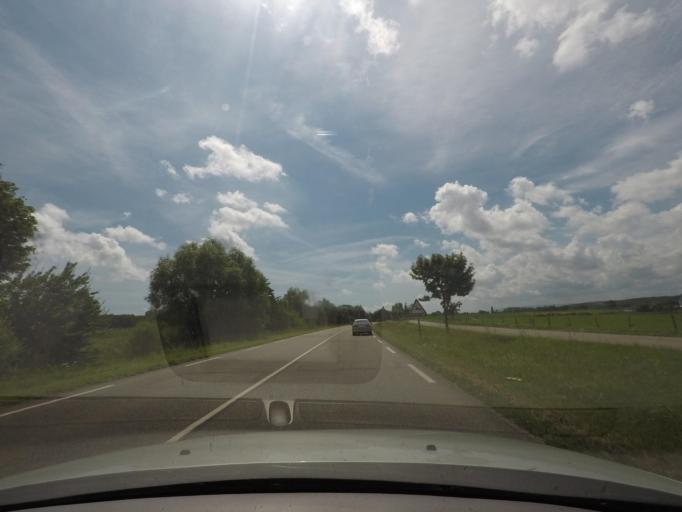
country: FR
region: Alsace
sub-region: Departement du Bas-Rhin
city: Drulingen
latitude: 48.8554
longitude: 7.2017
